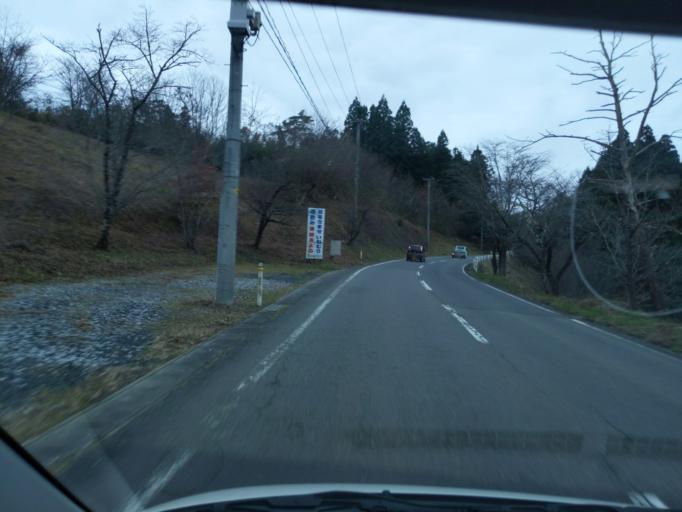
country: JP
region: Iwate
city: Mizusawa
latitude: 39.0330
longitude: 141.3375
